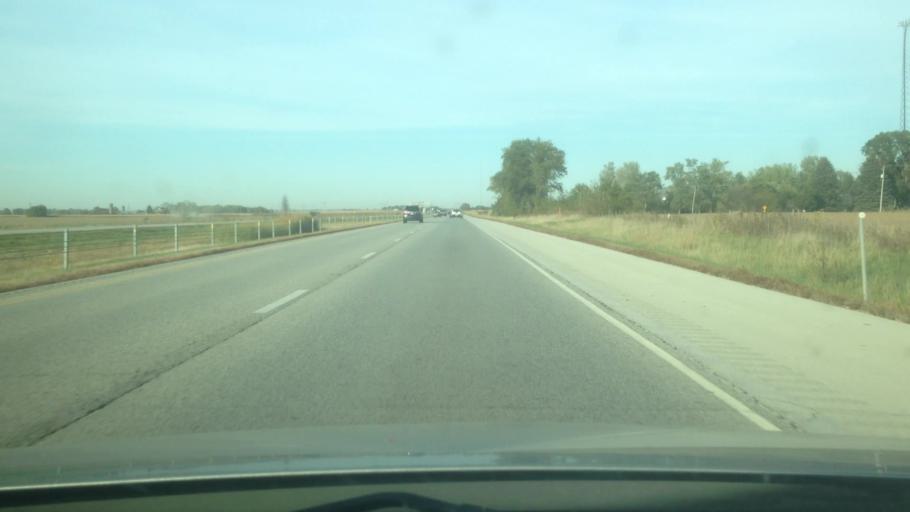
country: US
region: Illinois
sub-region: Kankakee County
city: Manteno
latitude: 41.2736
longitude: -87.8410
